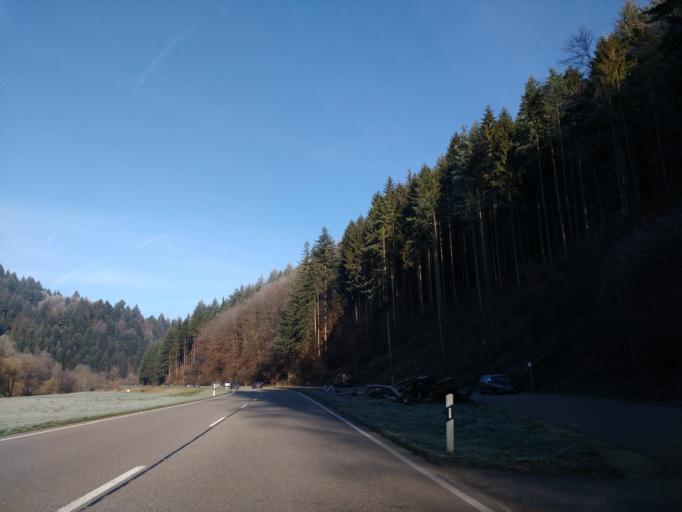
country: DE
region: Baden-Wuerttemberg
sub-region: Freiburg Region
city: Oppenau
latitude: 48.4992
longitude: 8.1395
